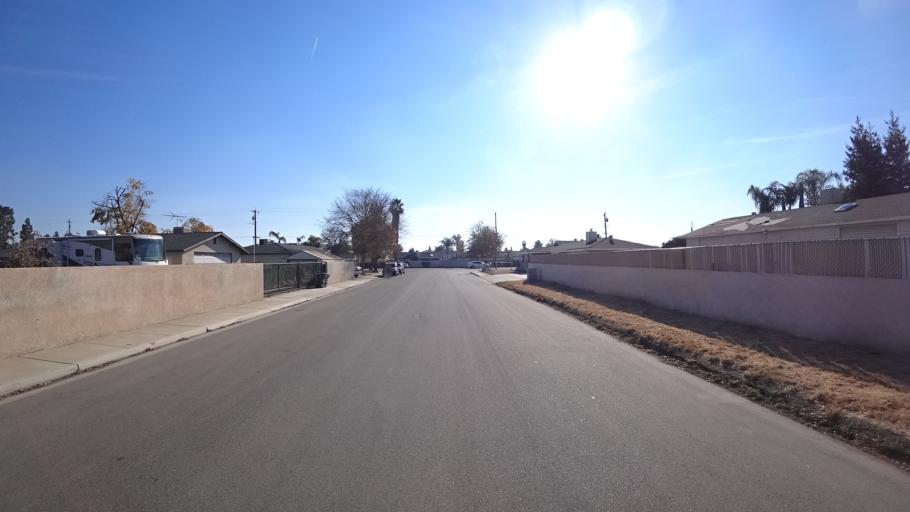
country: US
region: California
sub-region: Kern County
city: Greenfield
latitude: 35.3039
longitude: -119.0549
